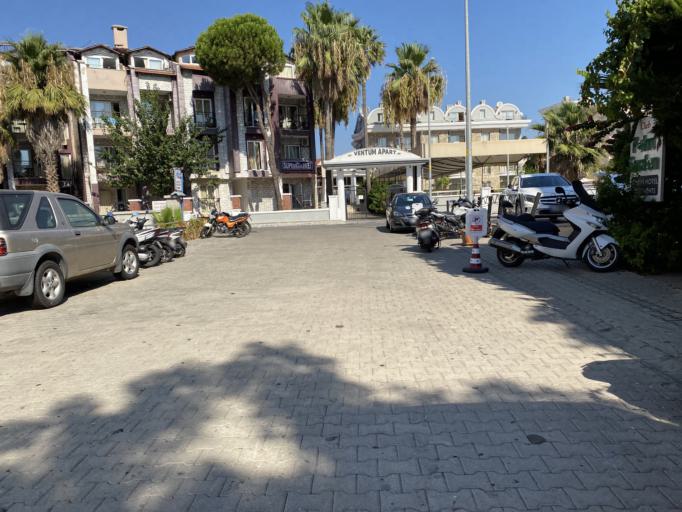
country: TR
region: Mugla
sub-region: Marmaris
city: Marmaris
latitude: 36.8450
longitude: 28.2519
